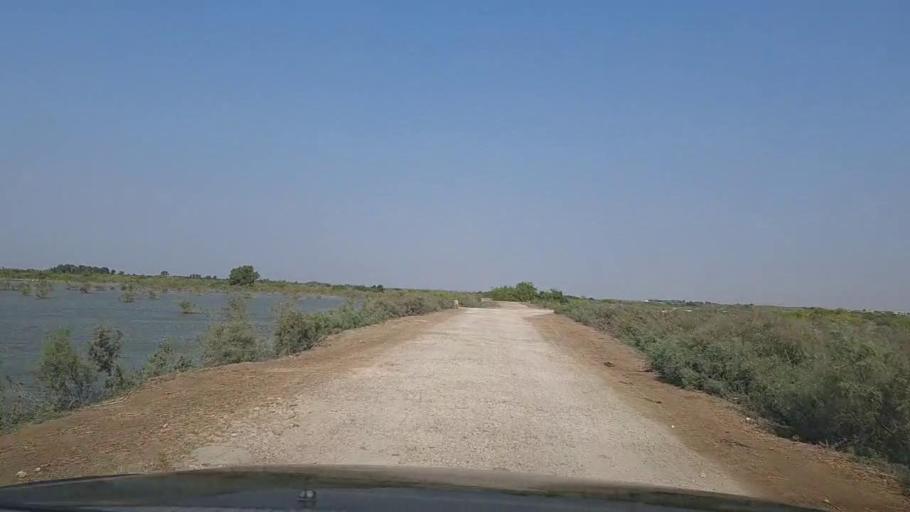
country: PK
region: Sindh
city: Thatta
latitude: 24.6397
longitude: 67.8143
